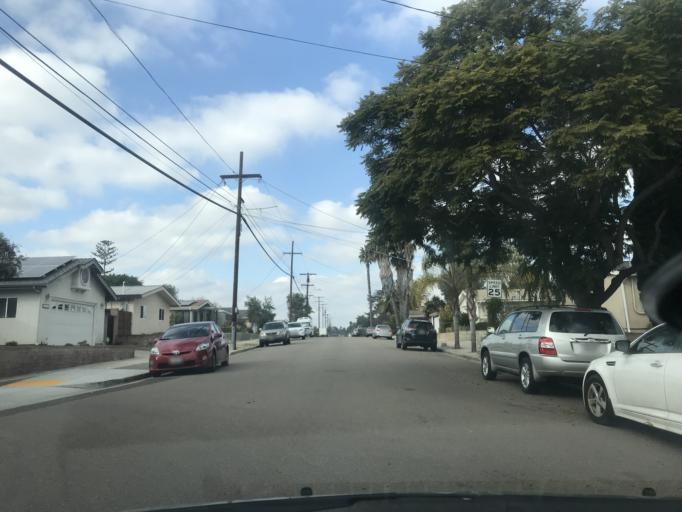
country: US
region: California
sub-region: San Diego County
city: San Diego
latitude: 32.7955
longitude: -117.1237
